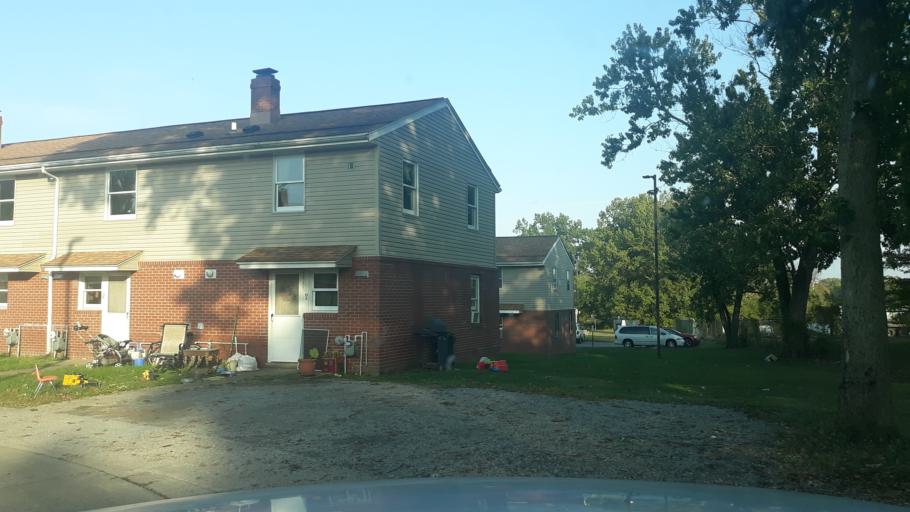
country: US
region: Illinois
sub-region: Saline County
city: Harrisburg
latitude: 37.7194
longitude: -88.5521
